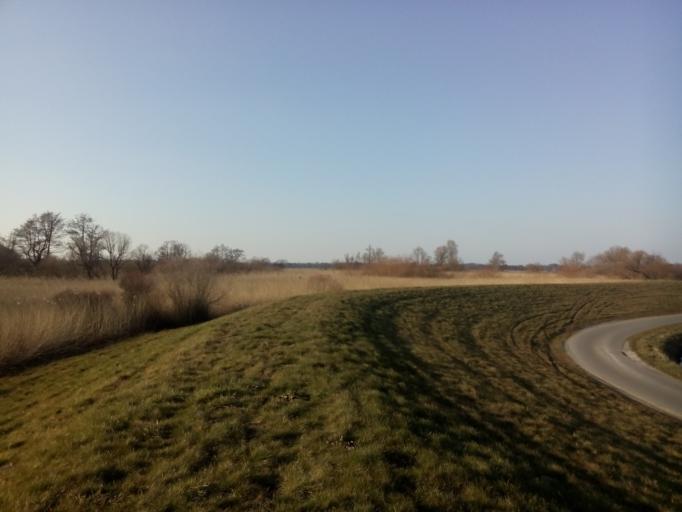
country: DE
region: Lower Saxony
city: Osterholz-Scharmbeck
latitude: 53.1615
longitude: 8.8296
